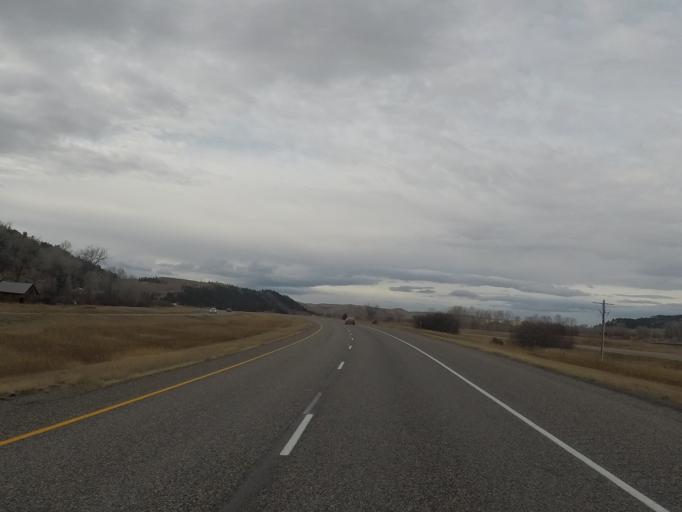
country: US
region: Montana
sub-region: Stillwater County
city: Absarokee
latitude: 45.7111
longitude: -109.5862
